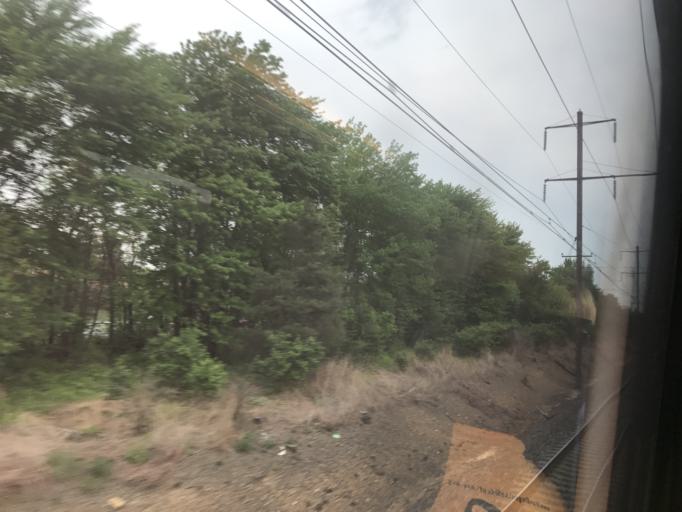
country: US
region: Maryland
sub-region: Prince George's County
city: Landover
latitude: 38.9333
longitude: -76.8923
